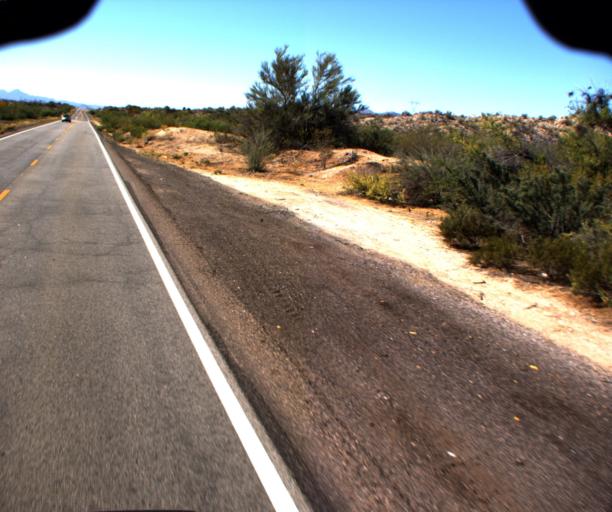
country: US
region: Arizona
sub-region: Yavapai County
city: Bagdad
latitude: 34.7738
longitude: -113.6215
